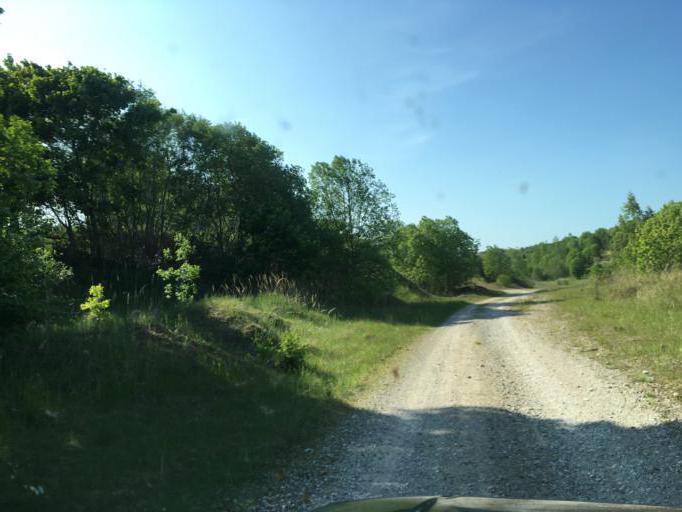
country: LV
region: Dundaga
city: Dundaga
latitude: 57.6105
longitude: 22.4417
